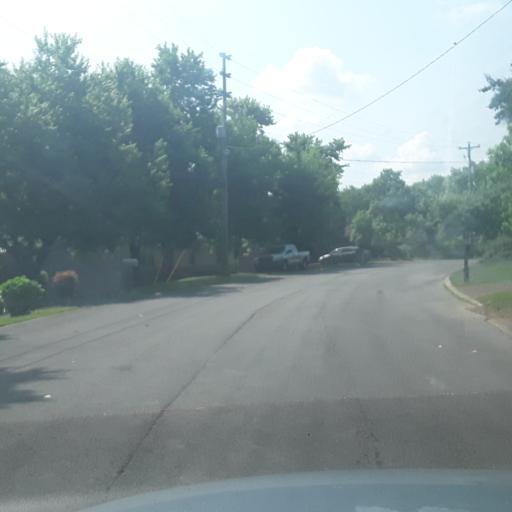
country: US
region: Tennessee
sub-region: Williamson County
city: Brentwood Estates
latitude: 36.0370
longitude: -86.7077
